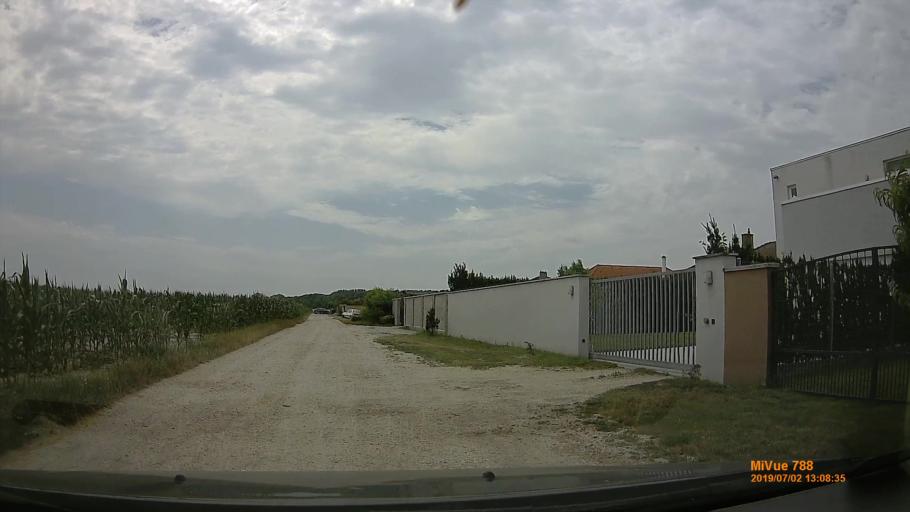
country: HU
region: Gyor-Moson-Sopron
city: Halaszi
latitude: 47.8561
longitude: 17.3271
